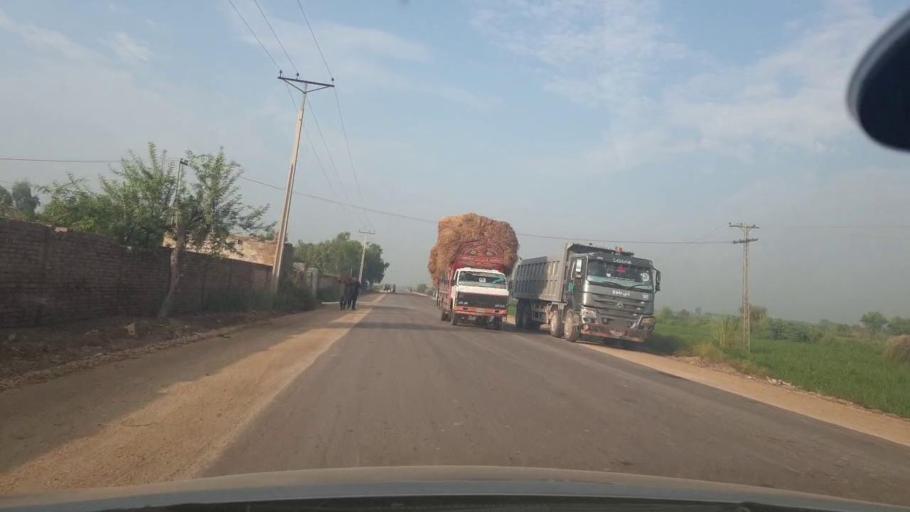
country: PK
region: Sindh
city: Jacobabad
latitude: 28.2590
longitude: 68.4130
